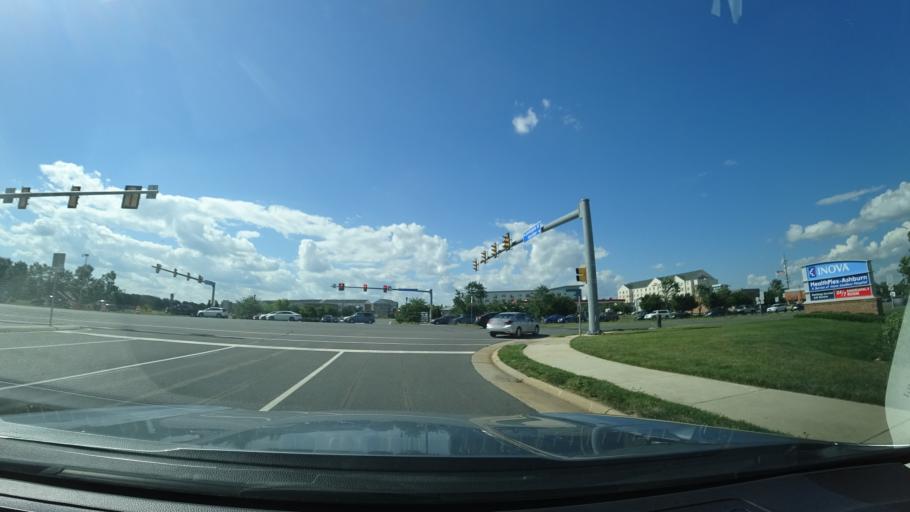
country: US
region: Virginia
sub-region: Loudoun County
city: Broadlands
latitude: 38.9951
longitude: -77.4822
